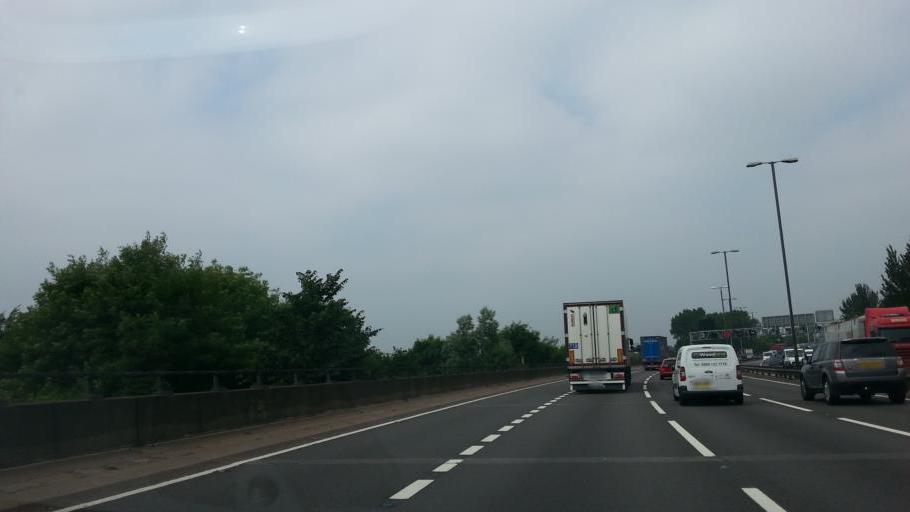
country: GB
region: England
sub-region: Sandwell
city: Wednesbury
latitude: 52.5690
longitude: -2.0096
